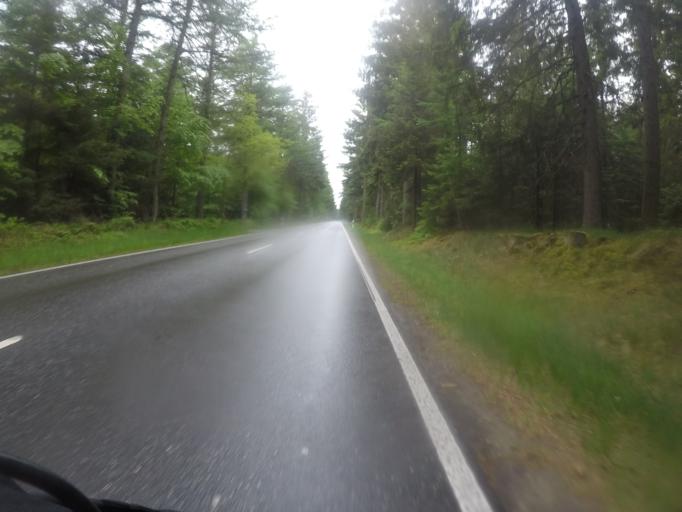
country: DE
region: Schleswig-Holstein
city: Hartenholm
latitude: 53.9256
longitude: 10.0900
